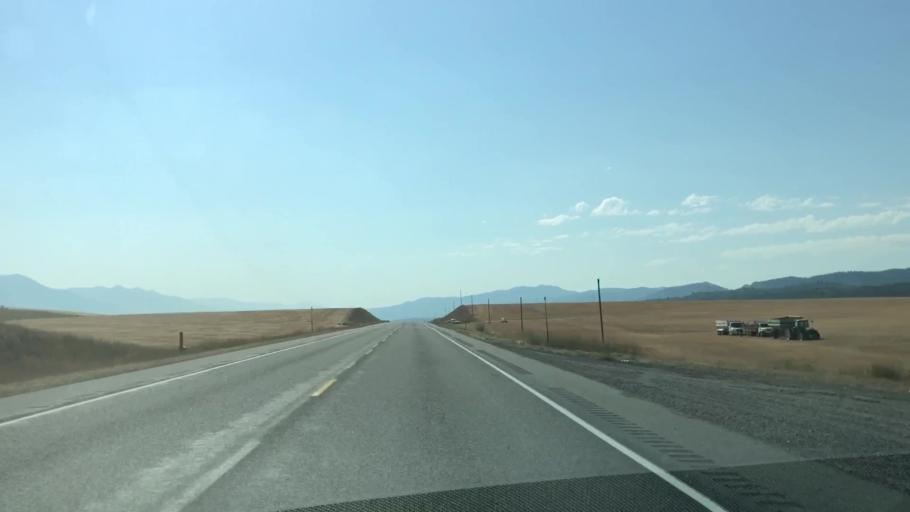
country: US
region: Idaho
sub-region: Teton County
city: Victor
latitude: 43.5131
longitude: -111.4817
